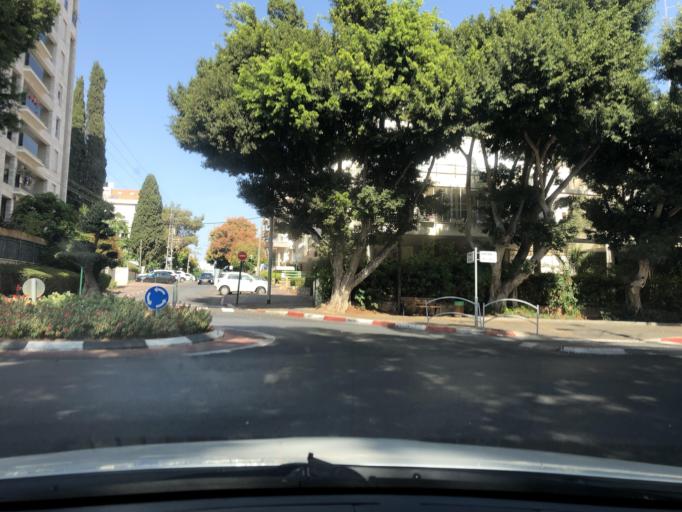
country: IL
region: Central District
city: Kfar Saba
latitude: 32.1744
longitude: 34.8992
